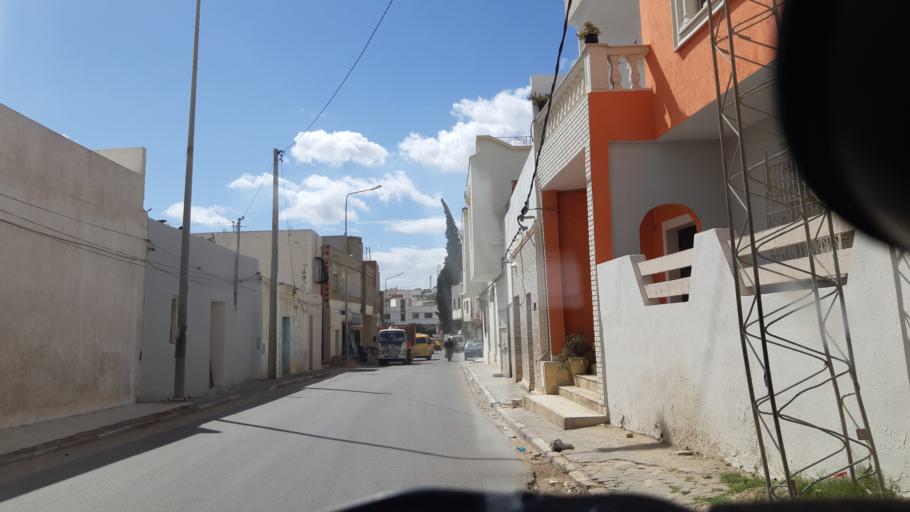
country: TN
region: Susah
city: Akouda
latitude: 35.8777
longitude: 10.5367
